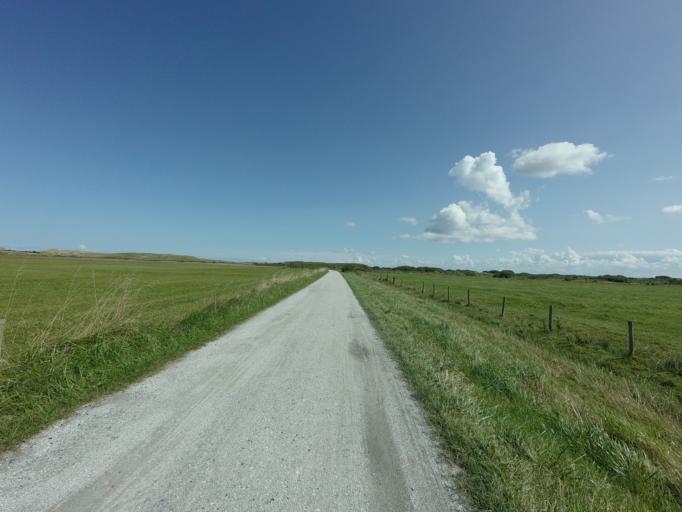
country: NL
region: Friesland
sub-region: Gemeente Terschelling
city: West-Terschelling
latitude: 53.4189
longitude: 5.3901
